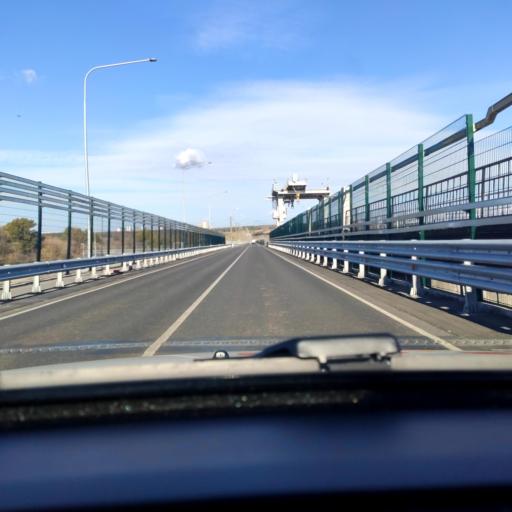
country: RU
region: Voronezj
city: Shilovo
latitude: 51.5388
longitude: 39.1383
